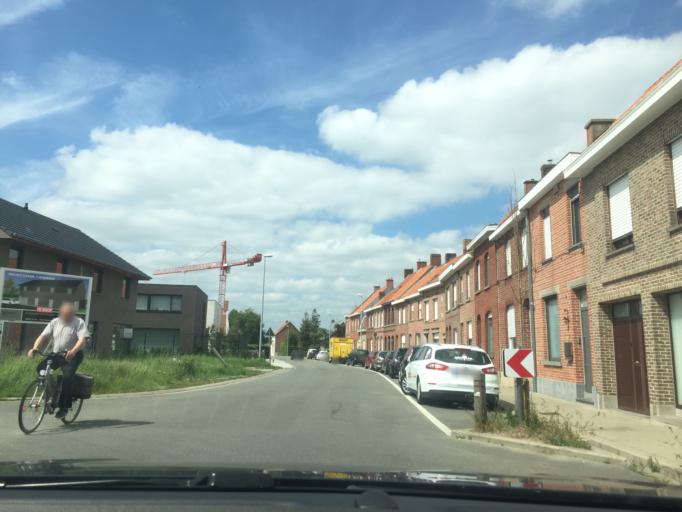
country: BE
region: Flanders
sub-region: Provincie West-Vlaanderen
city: Izegem
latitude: 50.9095
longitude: 3.2304
